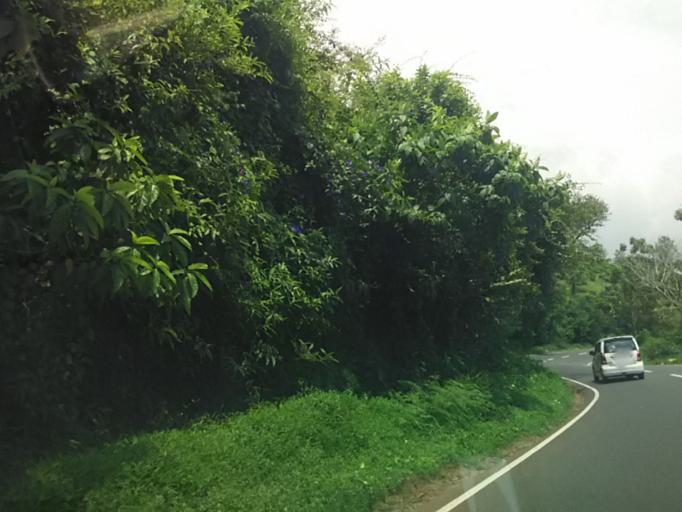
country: IN
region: Kerala
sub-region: Wayanad
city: Kalpetta
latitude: 11.5737
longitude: 76.0459
